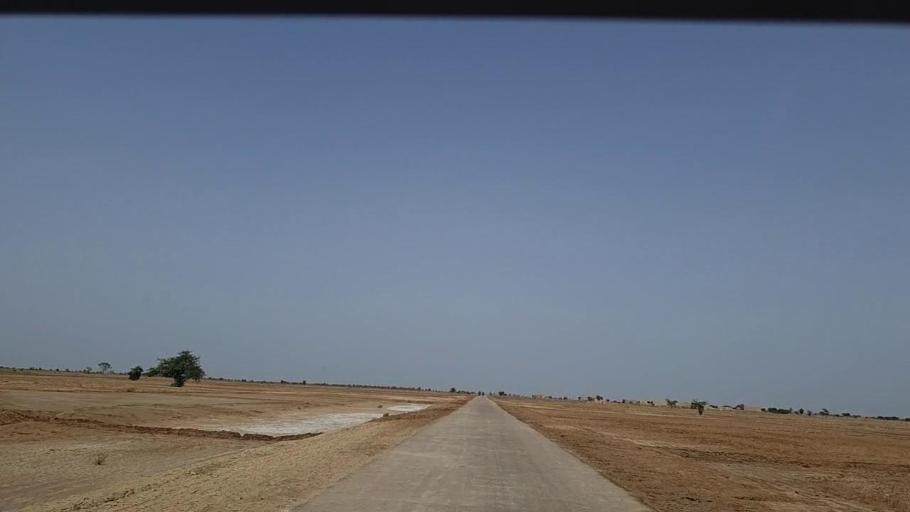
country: PK
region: Sindh
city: Johi
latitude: 26.7706
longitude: 67.6400
